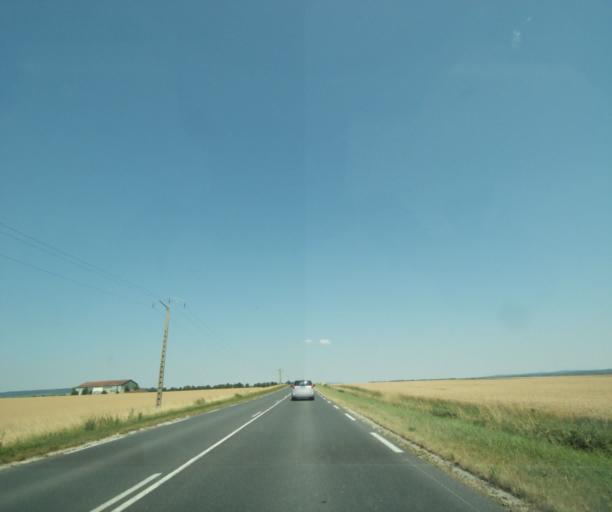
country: FR
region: Champagne-Ardenne
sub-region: Departement de la Marne
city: Mourmelon-le-Grand
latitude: 49.0812
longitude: 4.2820
